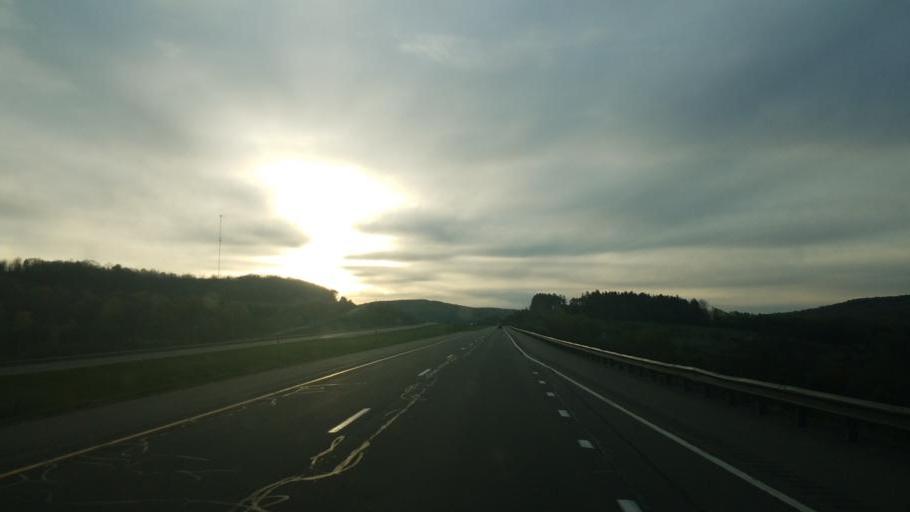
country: US
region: New York
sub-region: Allegany County
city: Cuba
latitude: 42.2249
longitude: -78.2708
